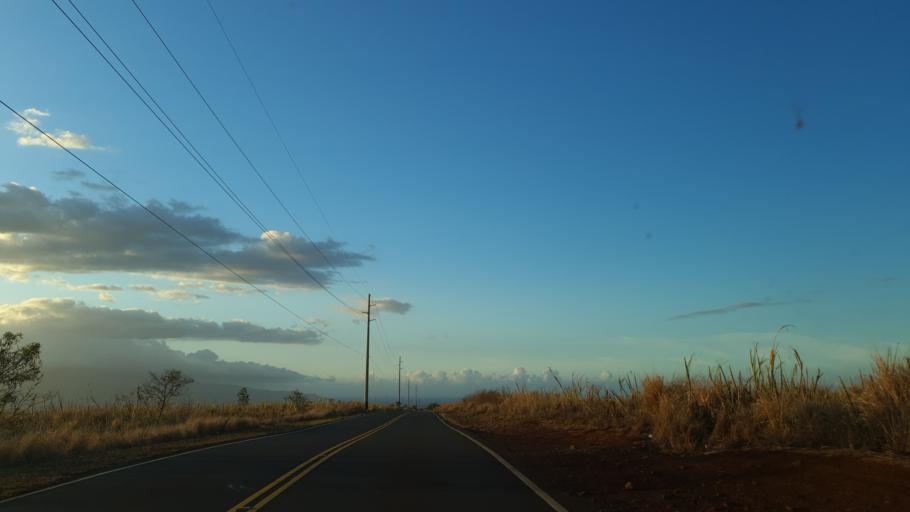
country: US
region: Hawaii
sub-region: Maui County
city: Pukalani
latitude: 20.8076
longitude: -156.3802
